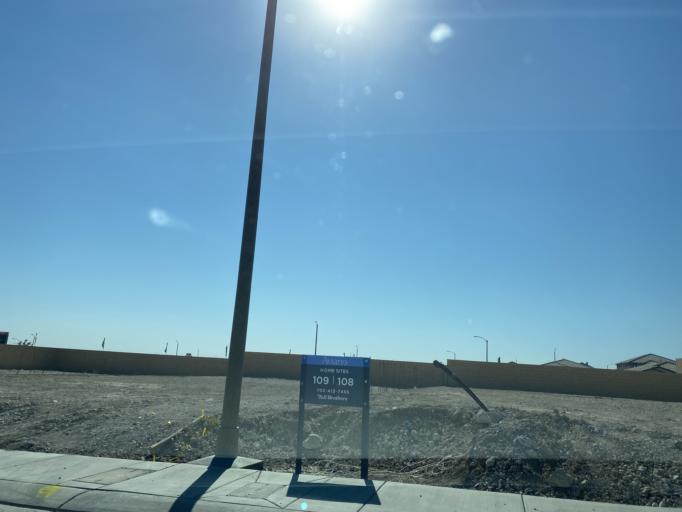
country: US
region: Nevada
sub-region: Clark County
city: Summerlin South
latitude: 36.3178
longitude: -115.3137
